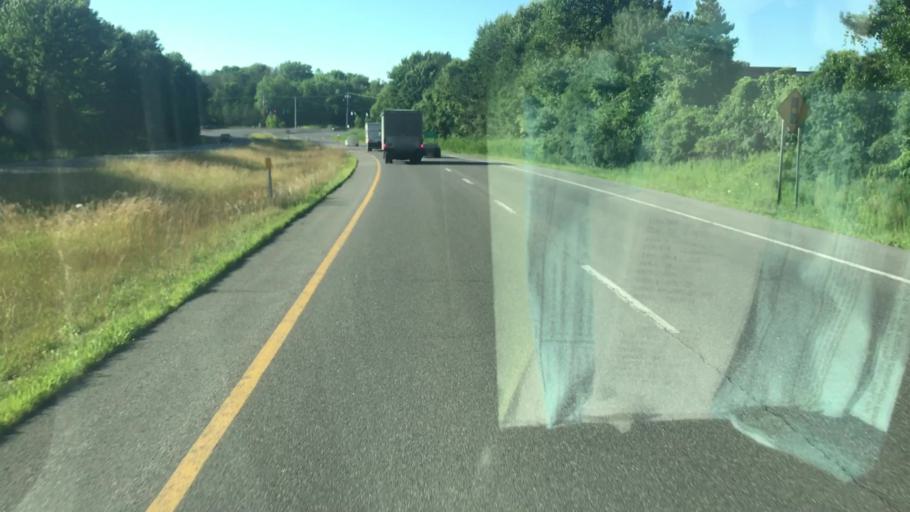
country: US
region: New York
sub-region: Onondaga County
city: Liverpool
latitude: 43.1388
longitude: -76.2080
